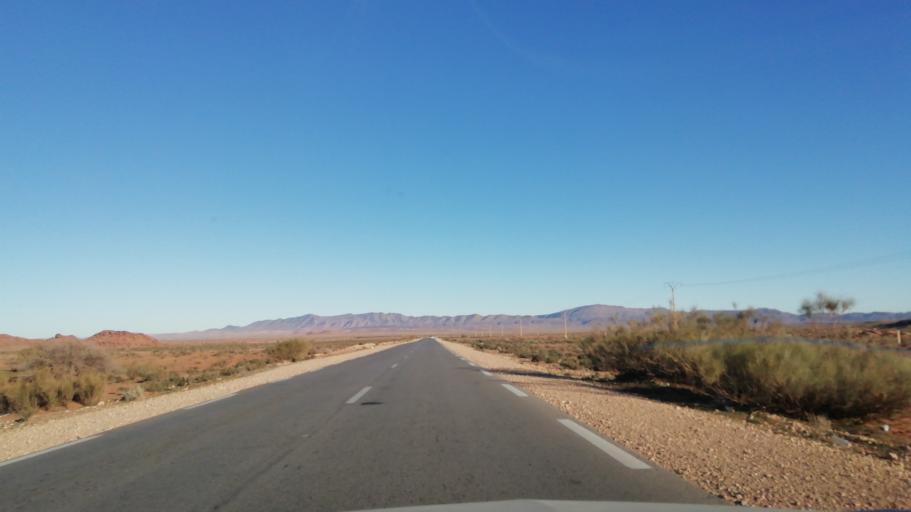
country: DZ
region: El Bayadh
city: El Abiodh Sidi Cheikh
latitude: 33.1700
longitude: 0.5008
